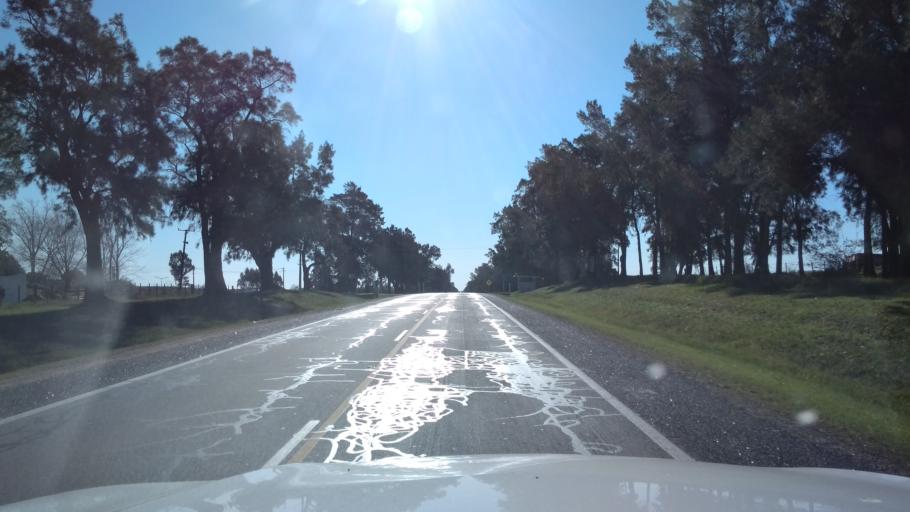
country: UY
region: Canelones
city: San Jacinto
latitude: -34.5901
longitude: -55.8365
